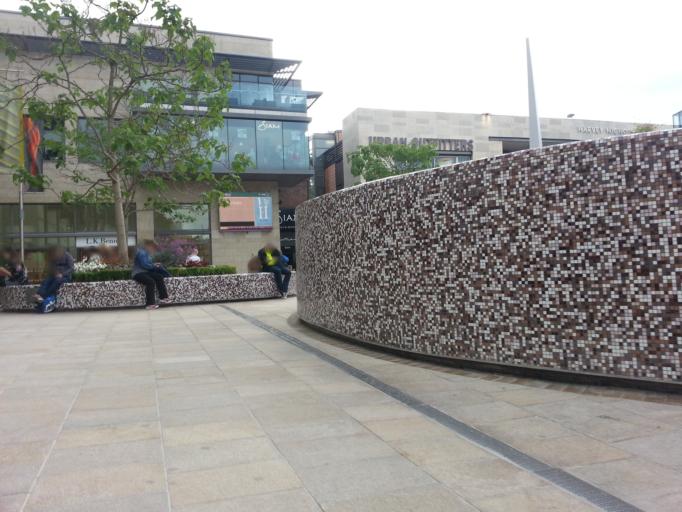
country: IE
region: Leinster
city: Dundrum
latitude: 53.2880
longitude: -6.2428
